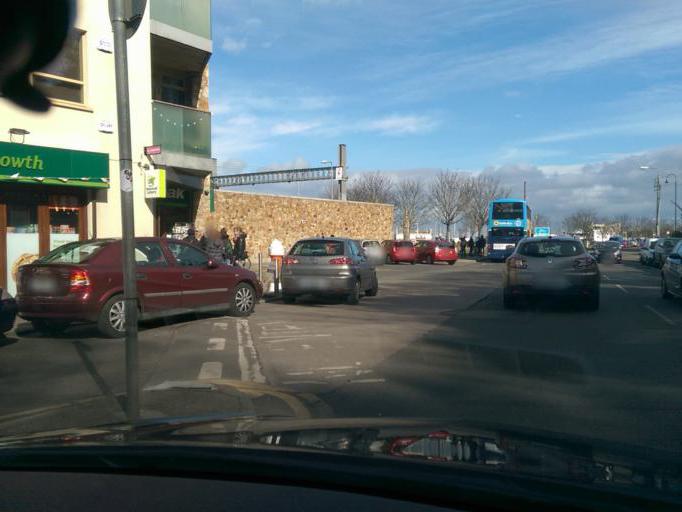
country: IE
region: Leinster
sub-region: Fingal County
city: Howth
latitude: 53.3888
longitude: -6.0739
